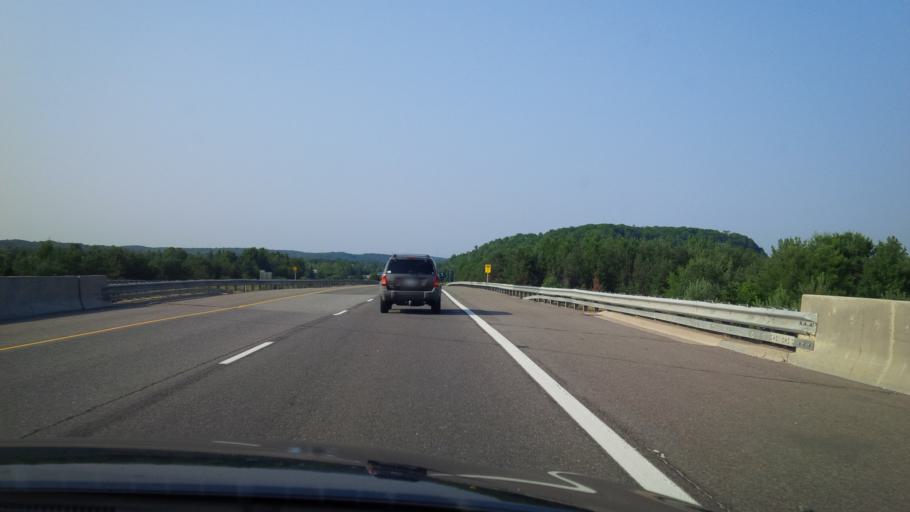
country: CA
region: Ontario
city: Huntsville
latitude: 45.3397
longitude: -79.2342
